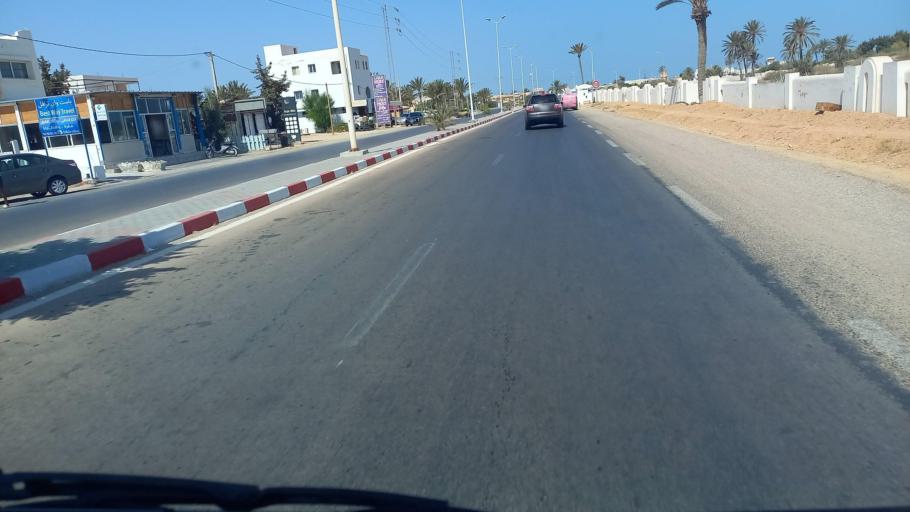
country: TN
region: Madanin
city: Midoun
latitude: 33.8614
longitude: 10.9673
